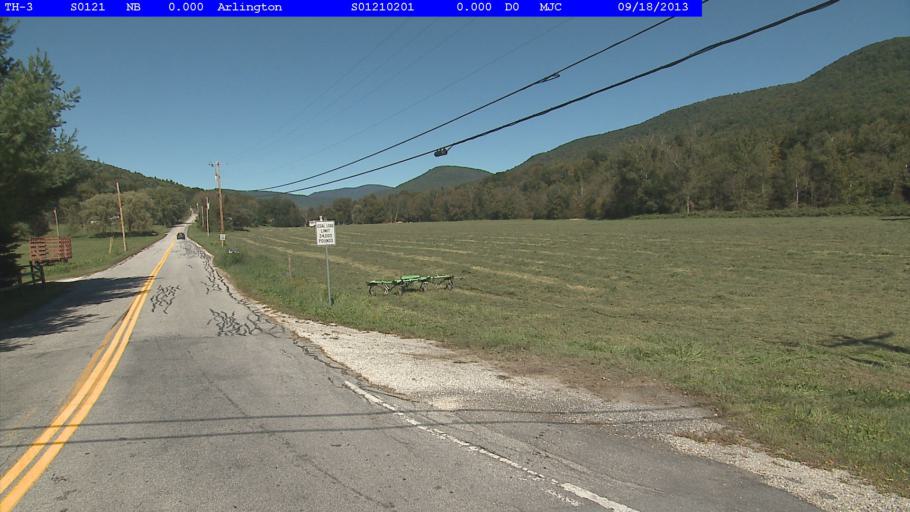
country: US
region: Vermont
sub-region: Bennington County
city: Arlington
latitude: 43.1035
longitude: -73.2127
